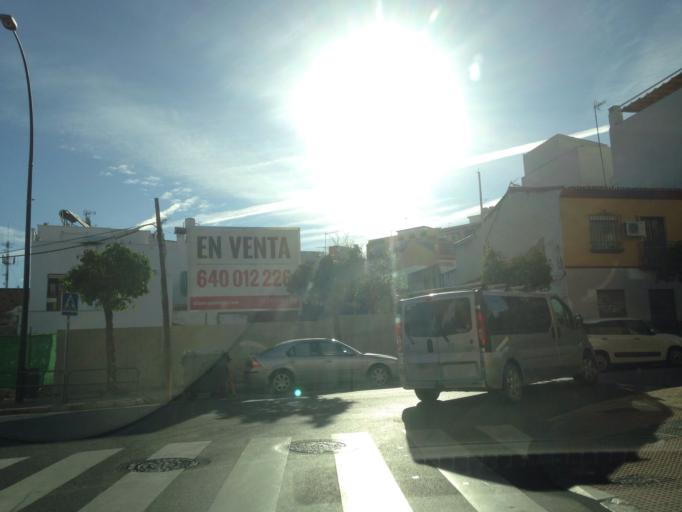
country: ES
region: Andalusia
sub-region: Provincia de Malaga
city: Malaga
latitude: 36.7305
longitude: -4.4216
